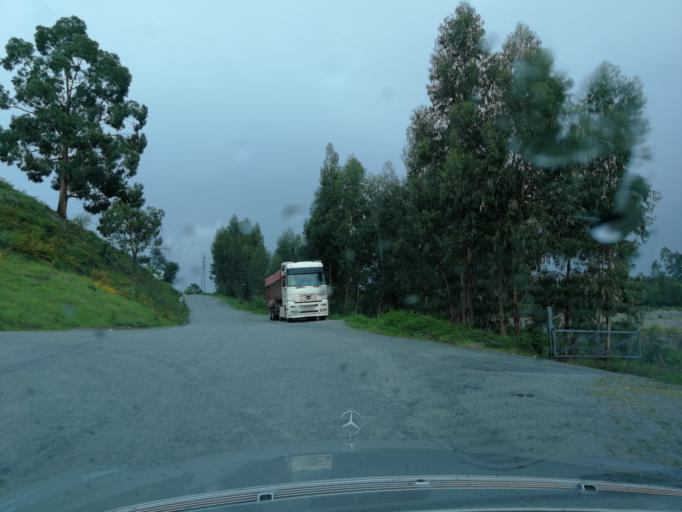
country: PT
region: Braga
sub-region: Vila Nova de Famalicao
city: Joane
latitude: 41.4611
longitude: -8.4340
